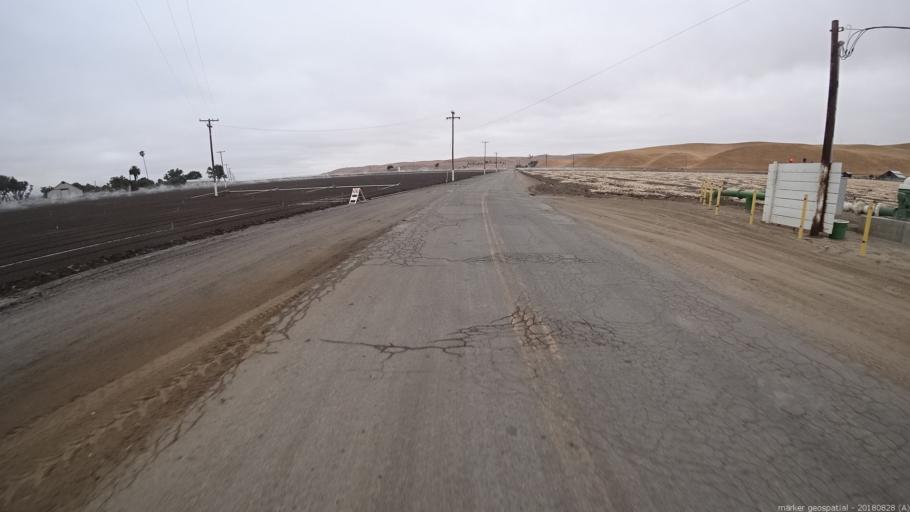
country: US
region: California
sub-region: San Luis Obispo County
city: Lake Nacimiento
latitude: 36.0089
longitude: -120.8862
